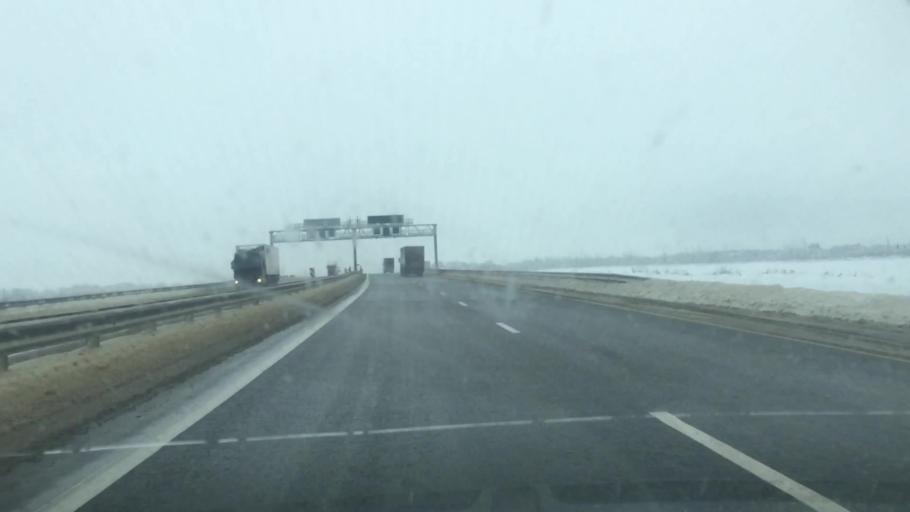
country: RU
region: Lipetsk
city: Stanovoye
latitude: 52.8964
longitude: 38.2283
